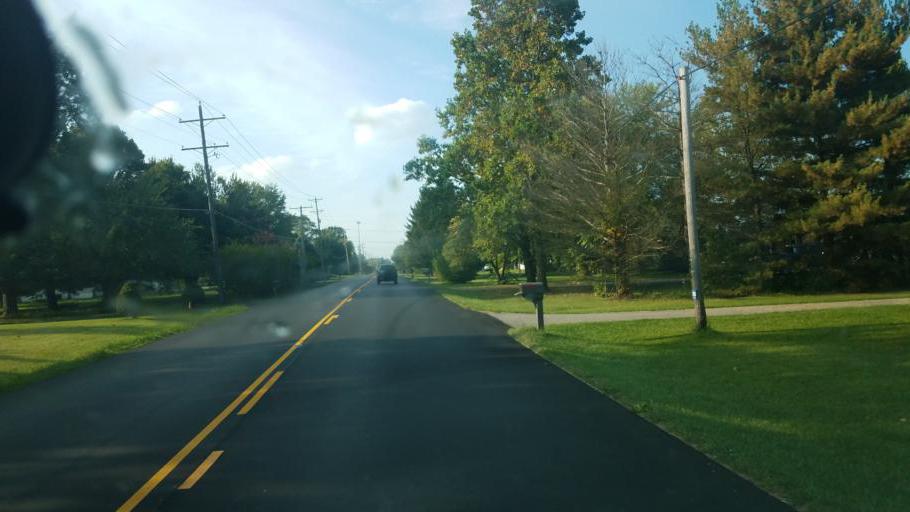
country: US
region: Ohio
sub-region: Franklin County
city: New Albany
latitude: 40.1029
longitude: -82.7787
